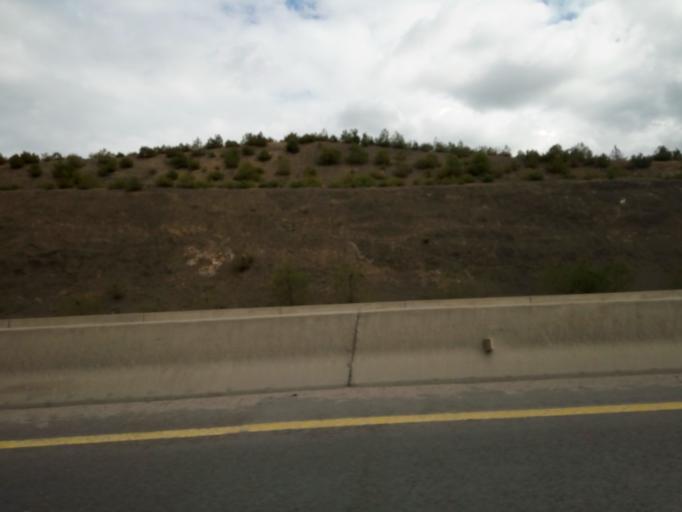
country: DZ
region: Bordj Bou Arreridj
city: Mansourah
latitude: 36.1944
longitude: 4.4361
